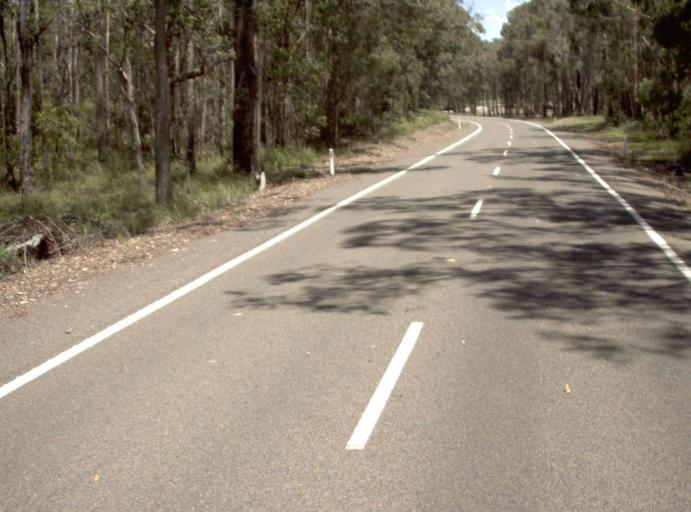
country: AU
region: Victoria
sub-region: East Gippsland
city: Lakes Entrance
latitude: -37.7733
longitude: 148.0535
